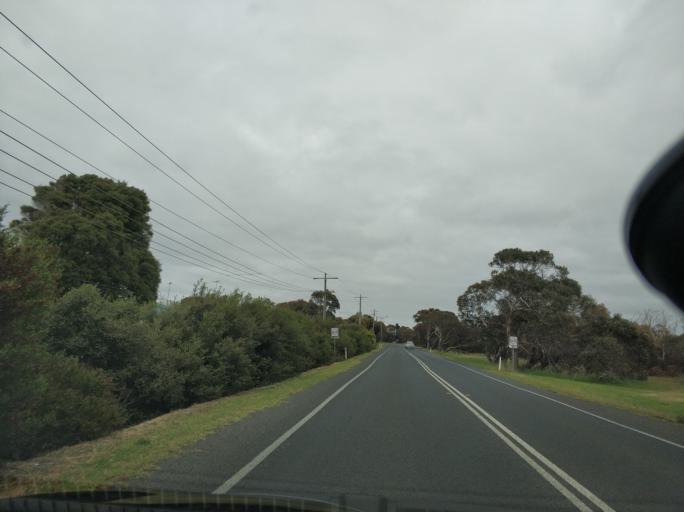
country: AU
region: Victoria
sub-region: Surf Coast
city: Anglesea
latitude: -38.3383
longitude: 144.3004
